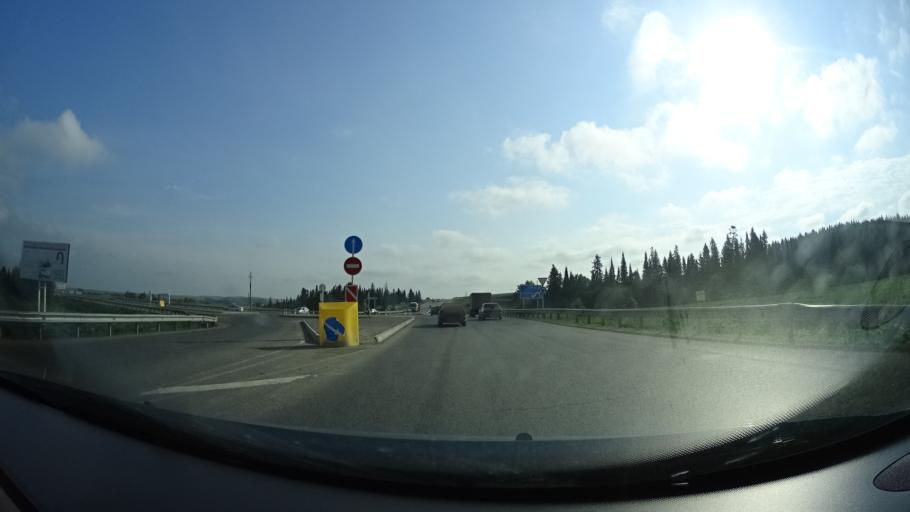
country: RU
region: Perm
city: Kultayevo
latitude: 57.8627
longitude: 55.8763
